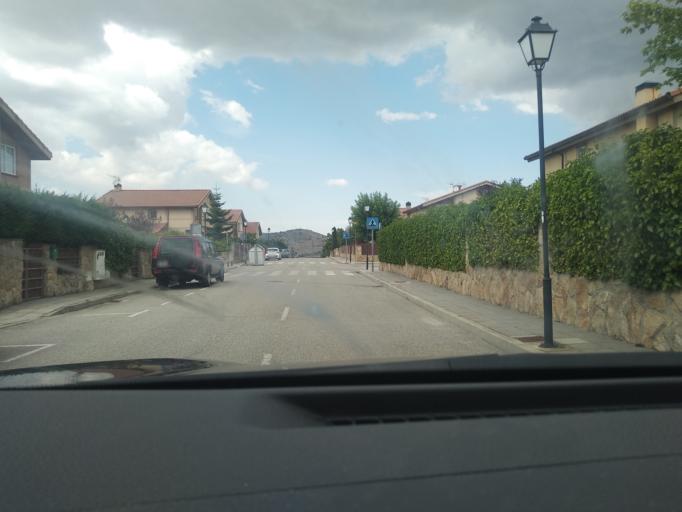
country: ES
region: Castille and Leon
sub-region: Provincia de Segovia
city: Otero de Herreros
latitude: 40.7409
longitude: -4.1875
